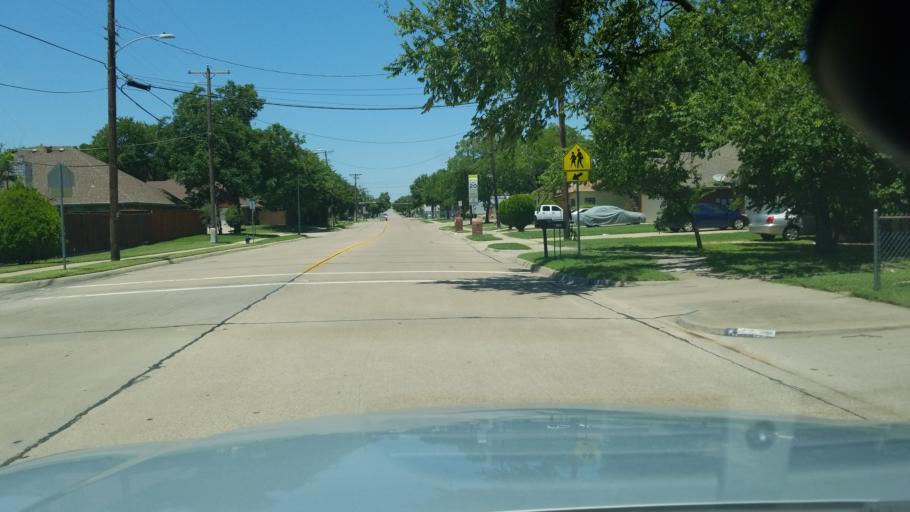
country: US
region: Texas
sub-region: Dallas County
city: Irving
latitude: 32.7987
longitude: -96.9257
